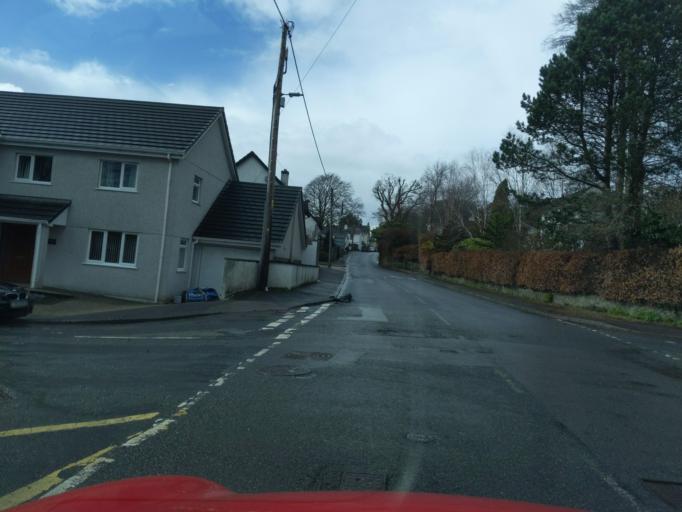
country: GB
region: England
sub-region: Devon
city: Tavistock
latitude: 50.5362
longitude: -4.1356
